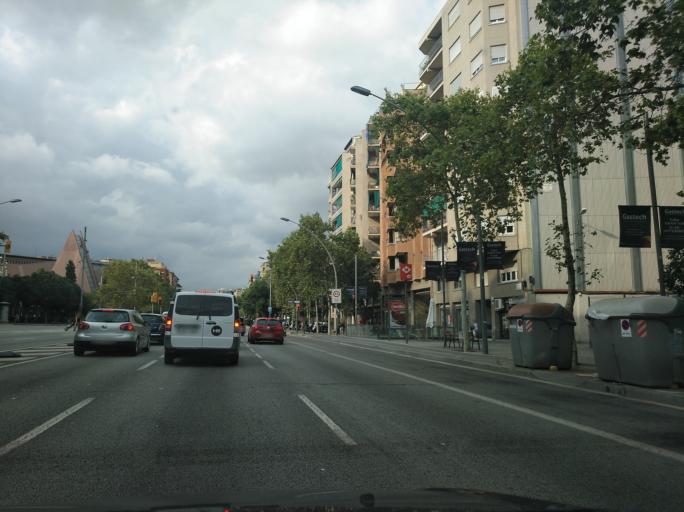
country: ES
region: Catalonia
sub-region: Provincia de Barcelona
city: Sant Marti
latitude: 41.4165
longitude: 2.1870
